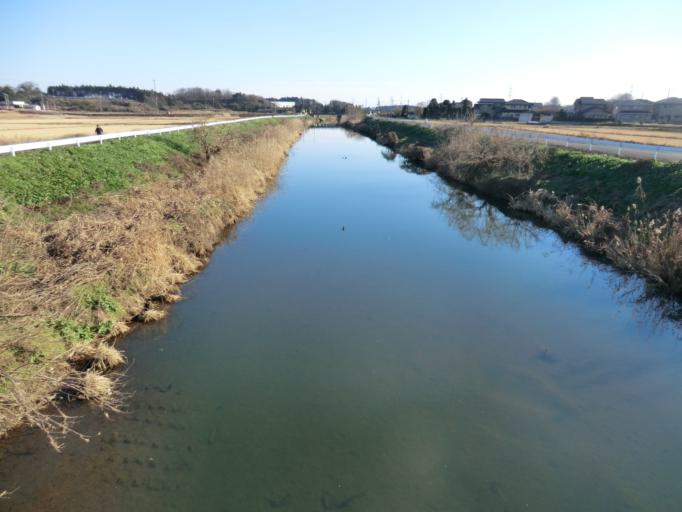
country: JP
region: Ibaraki
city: Ushiku
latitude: 36.0327
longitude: 140.0791
